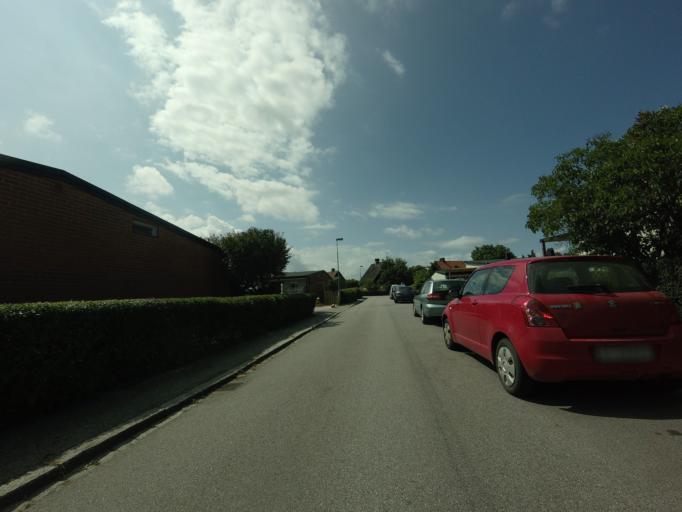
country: SE
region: Skane
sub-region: Malmo
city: Malmoe
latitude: 55.5693
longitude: 13.0019
